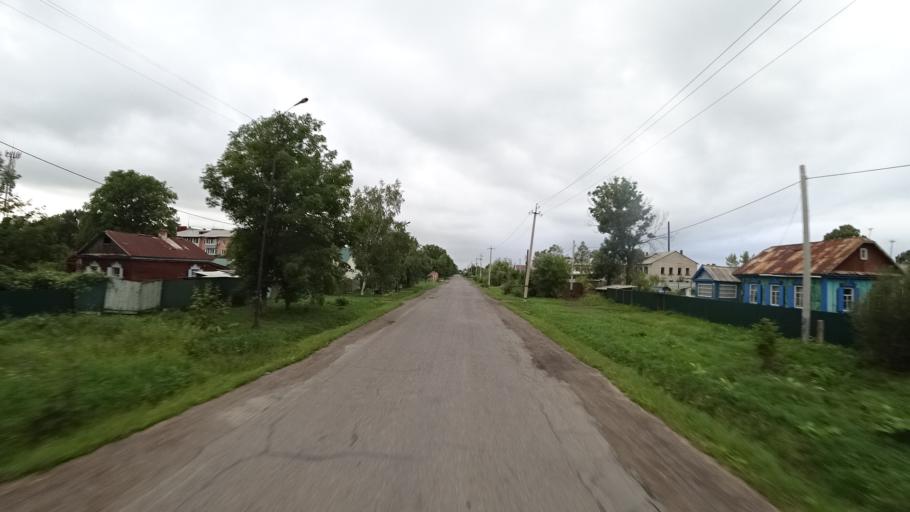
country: RU
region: Primorskiy
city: Chernigovka
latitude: 44.3453
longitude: 132.5771
